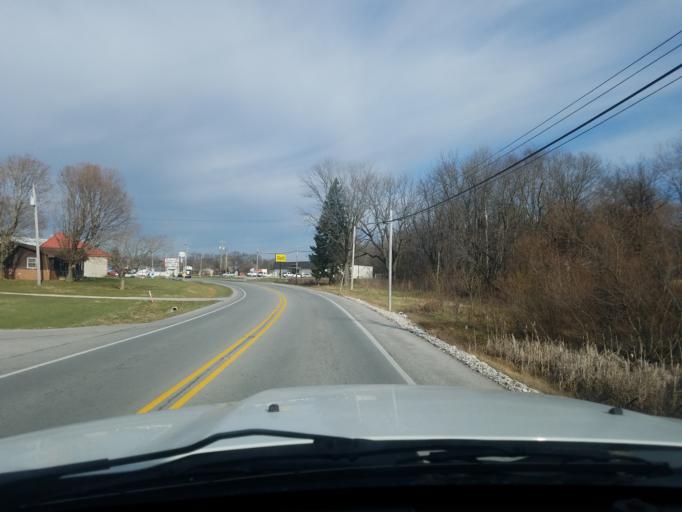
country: US
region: Indiana
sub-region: Orange County
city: Orleans
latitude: 38.6532
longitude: -86.4532
